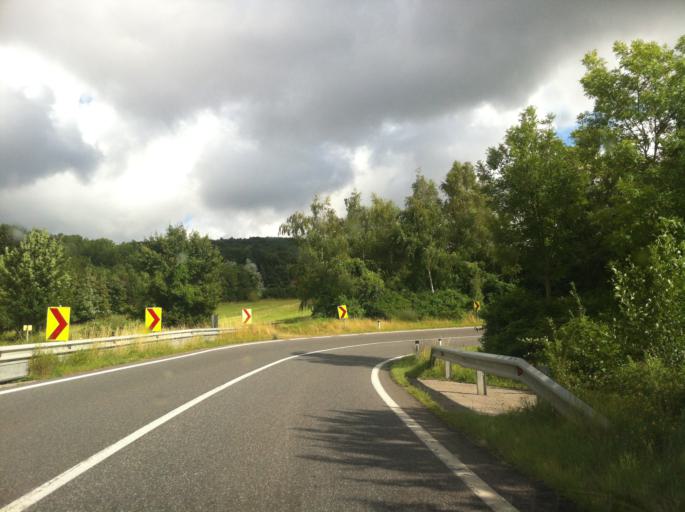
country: AT
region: Lower Austria
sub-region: Politischer Bezirk Tulln
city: Tulbing
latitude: 48.2579
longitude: 16.0862
